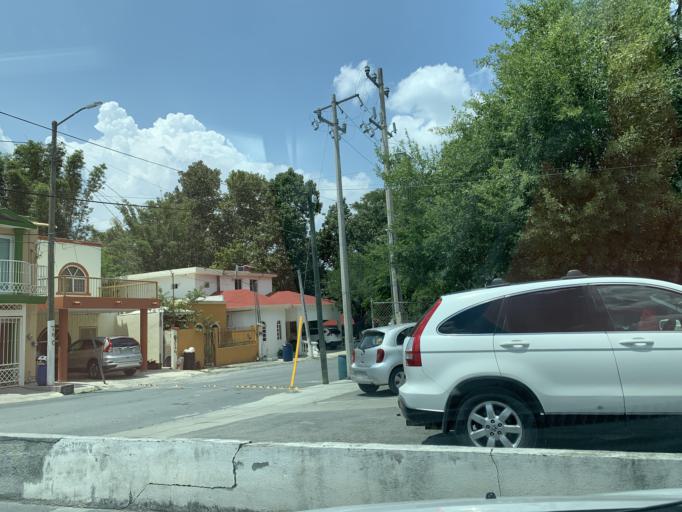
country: MX
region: Nuevo Leon
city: Santiago
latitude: 25.4009
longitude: -100.1304
